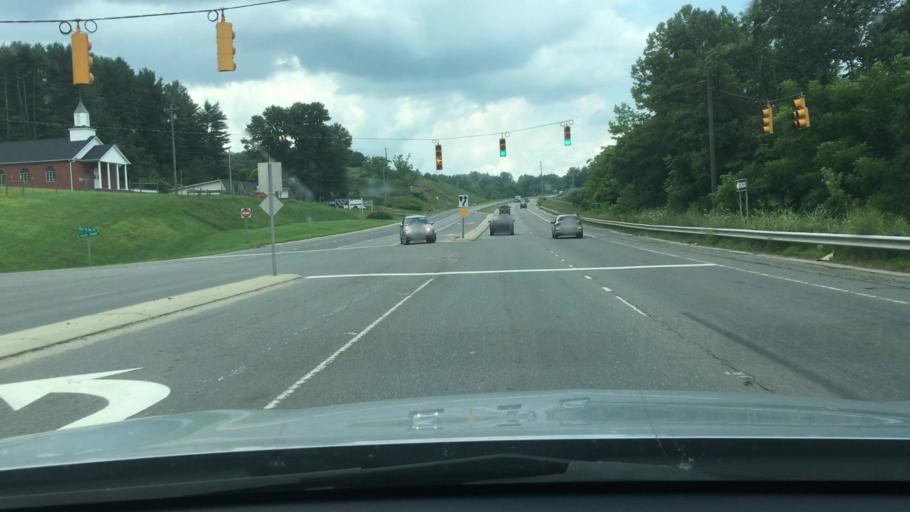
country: US
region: North Carolina
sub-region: Yancey County
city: Burnsville
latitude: 35.9118
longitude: -82.3478
